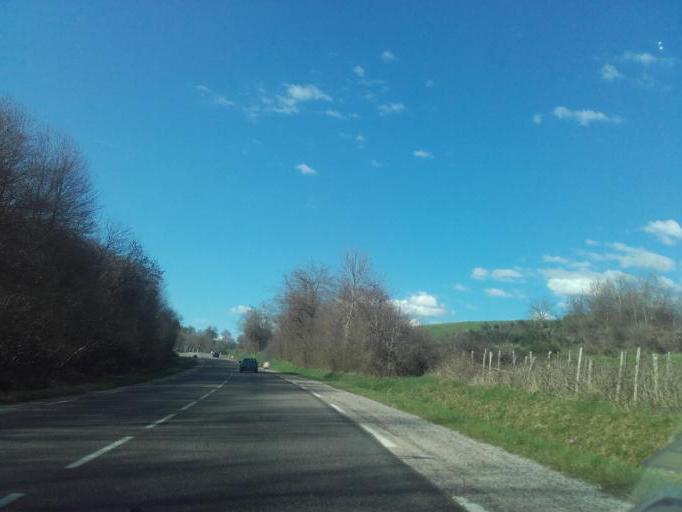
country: FR
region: Rhone-Alpes
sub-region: Departement de l'Isere
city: Champier
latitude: 45.4789
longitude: 5.2925
